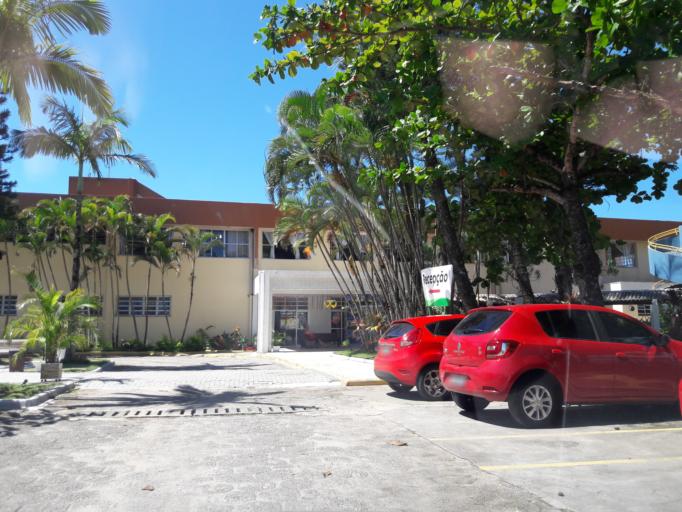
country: BR
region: Parana
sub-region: Pontal Do Parana
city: Pontal do Parana
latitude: -25.7042
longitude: -48.4734
